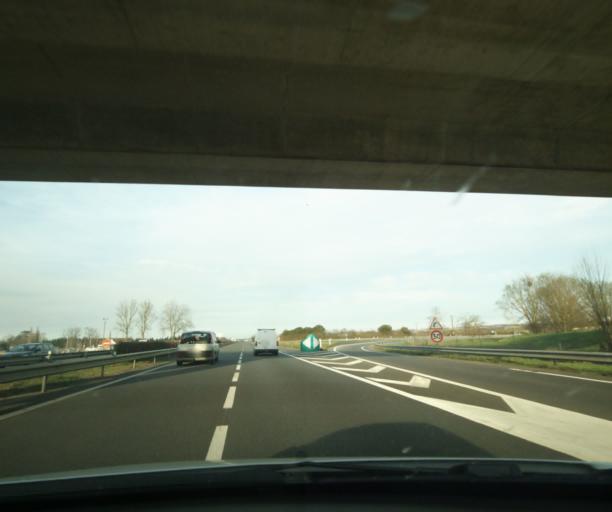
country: FR
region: Midi-Pyrenees
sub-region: Departement de la Haute-Garonne
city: Rieux-Volvestre
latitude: 43.2740
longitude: 1.1388
